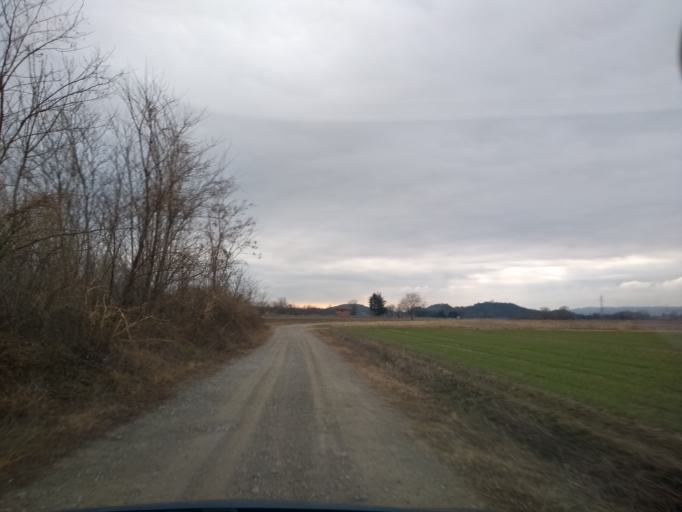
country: IT
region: Piedmont
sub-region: Provincia di Torino
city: Fiorano Canavese
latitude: 45.4855
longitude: 7.8408
